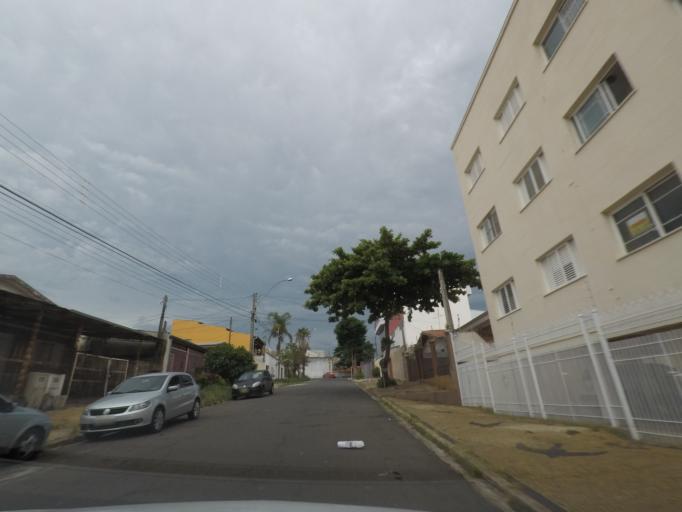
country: BR
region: Sao Paulo
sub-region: Campinas
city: Campinas
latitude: -22.9344
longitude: -47.0919
